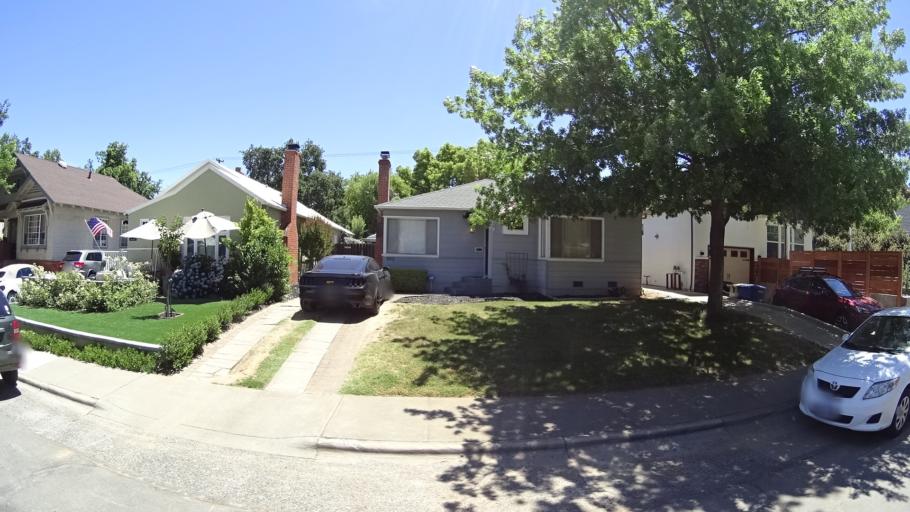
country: US
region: California
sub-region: Sacramento County
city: Sacramento
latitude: 38.5727
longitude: -121.4510
